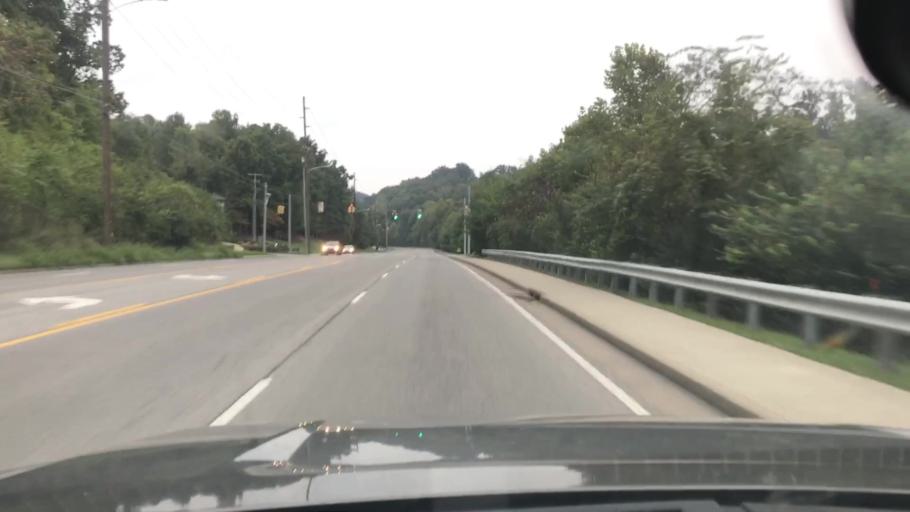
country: US
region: Tennessee
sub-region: Davidson County
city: Belle Meade
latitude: 36.0889
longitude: -86.9208
